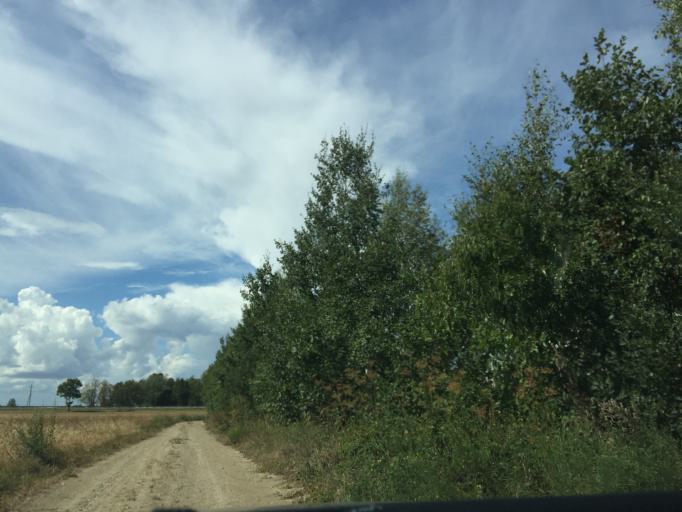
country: LT
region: Siauliu apskritis
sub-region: Joniskis
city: Joniskis
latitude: 56.2979
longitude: 23.6413
